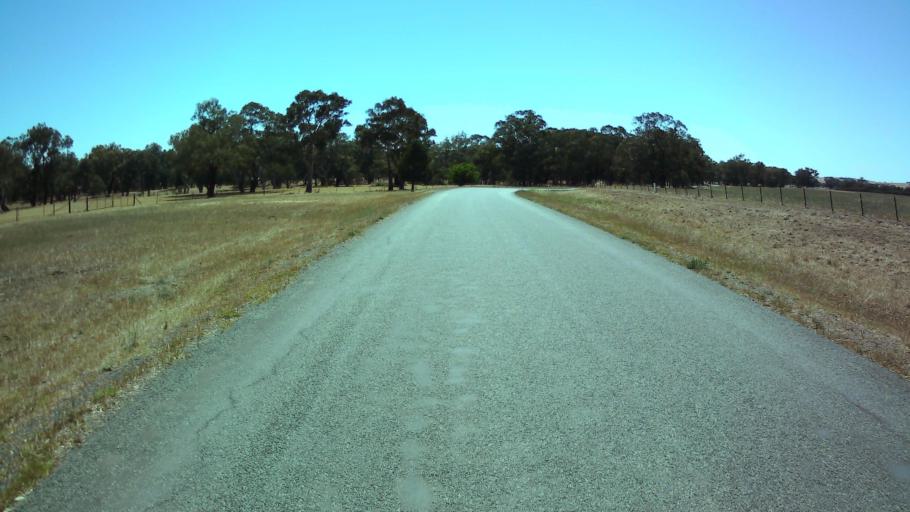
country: AU
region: New South Wales
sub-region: Weddin
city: Grenfell
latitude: -34.0006
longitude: 148.3909
